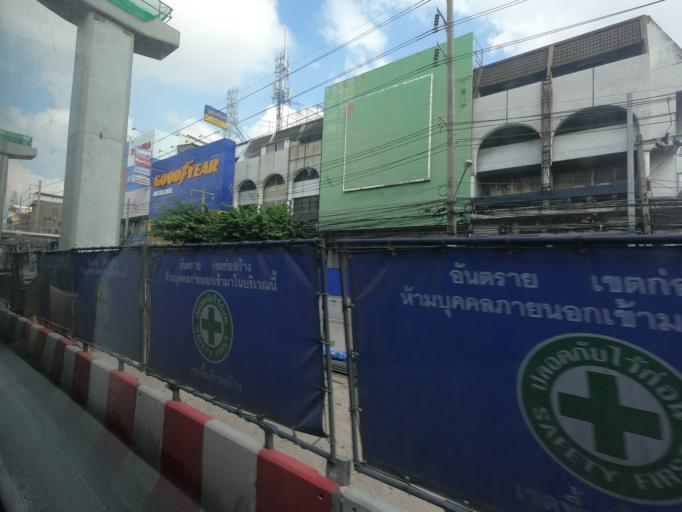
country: TH
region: Bangkok
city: Wang Thonglang
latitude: 13.7880
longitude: 100.6059
